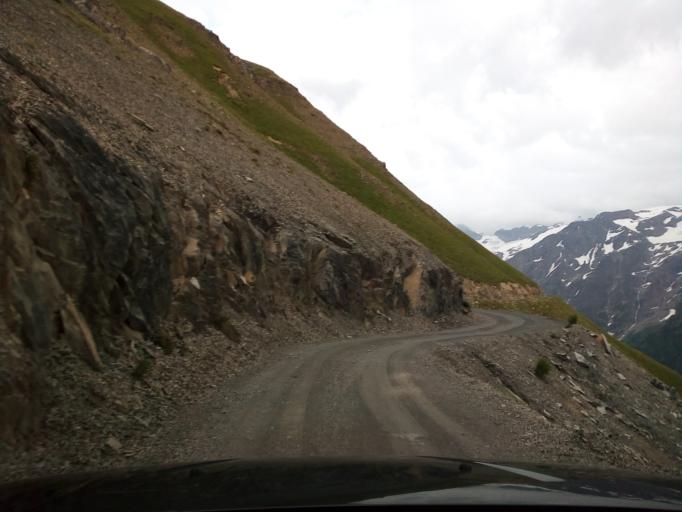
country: FR
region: Rhone-Alpes
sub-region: Departement de l'Isere
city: Mont-de-Lans
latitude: 45.0527
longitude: 6.1903
